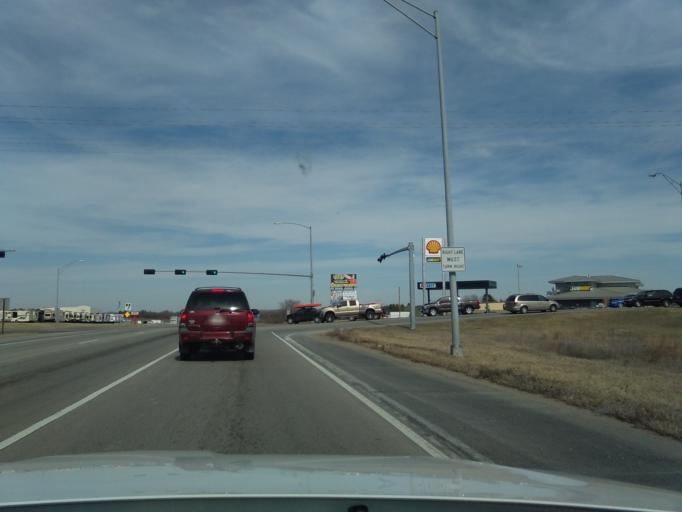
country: US
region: Nebraska
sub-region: Lancaster County
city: Hickman
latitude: 40.6968
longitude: -96.7052
